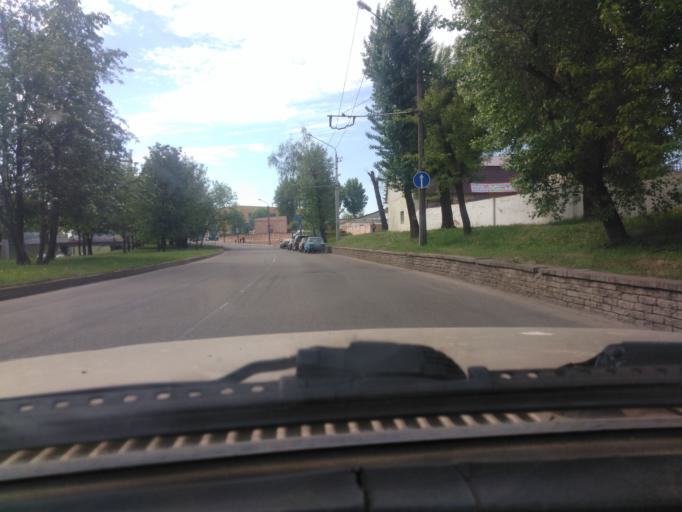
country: BY
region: Mogilev
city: Buynichy
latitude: 53.8938
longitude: 30.2978
